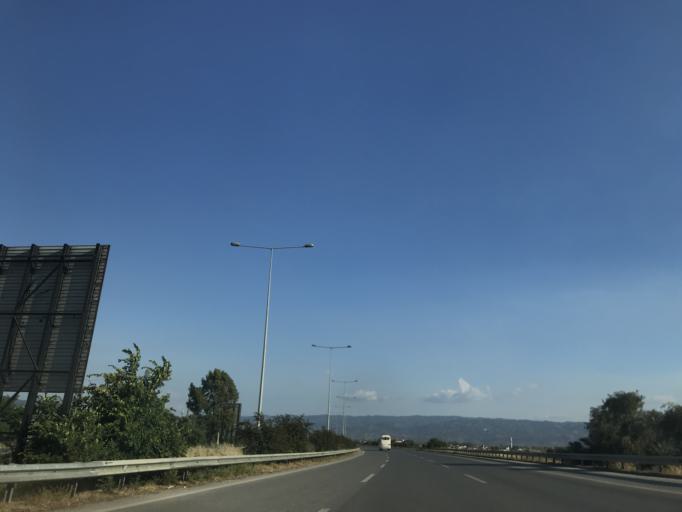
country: TR
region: Aydin
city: Aydin
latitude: 37.8328
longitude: 27.8100
